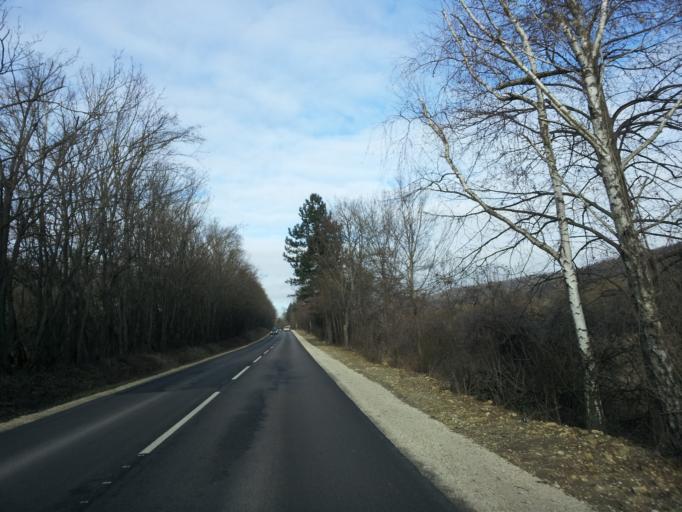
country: HU
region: Pest
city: Solymar
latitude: 47.5622
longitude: 18.9158
